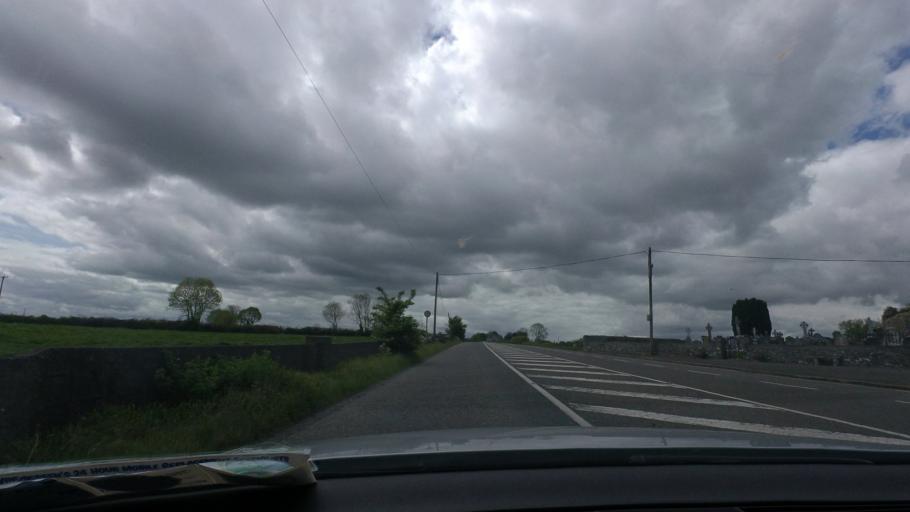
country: IE
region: Munster
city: Thurles
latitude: 52.6327
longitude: -7.7500
